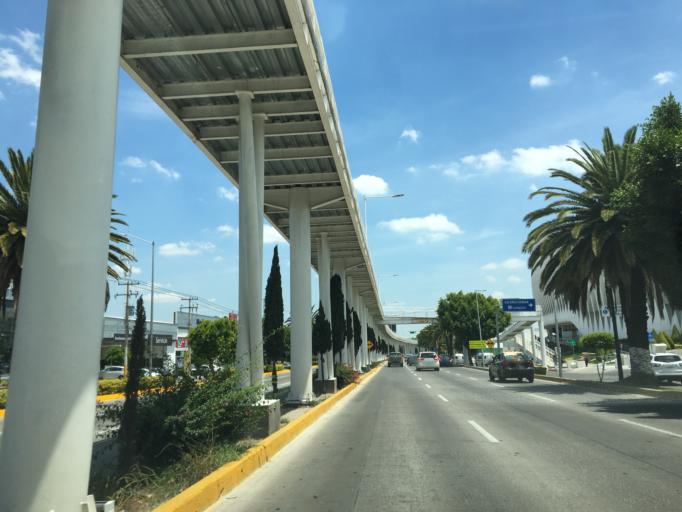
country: MX
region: Puebla
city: Puebla
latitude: 19.0699
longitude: -98.2257
